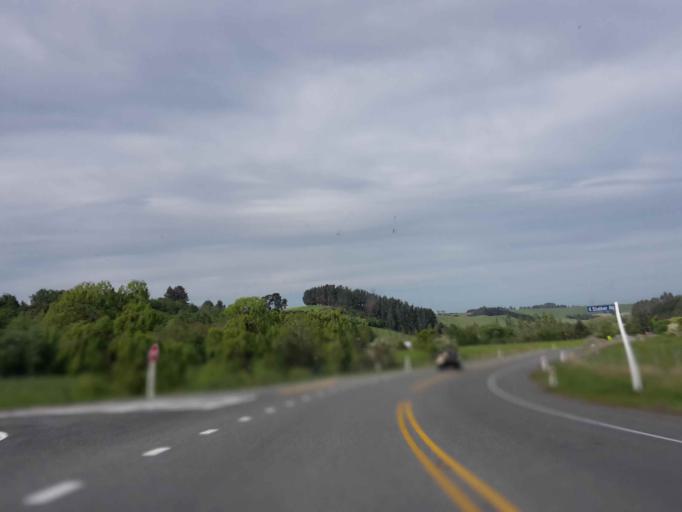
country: NZ
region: Canterbury
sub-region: Timaru District
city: Pleasant Point
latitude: -44.1115
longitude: 171.1366
